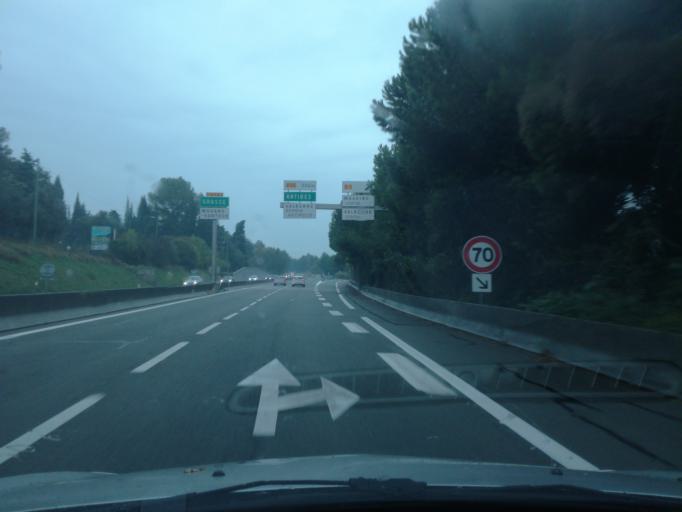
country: FR
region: Provence-Alpes-Cote d'Azur
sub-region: Departement des Alpes-Maritimes
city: Mougins
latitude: 43.5962
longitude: 7.0005
